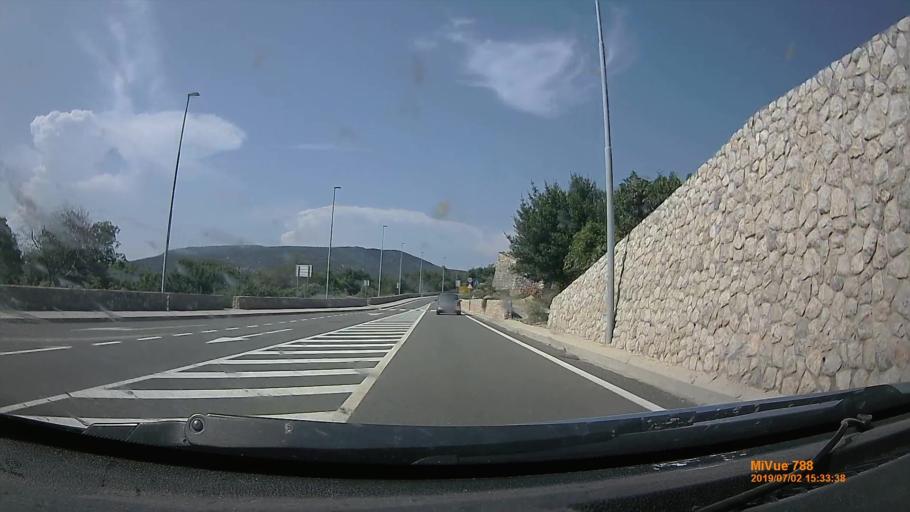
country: HR
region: Primorsko-Goranska
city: Cres
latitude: 44.9610
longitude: 14.4132
